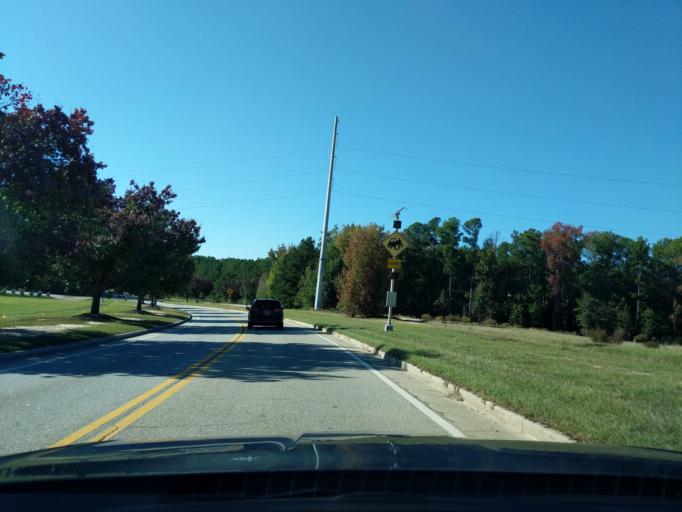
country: US
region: Georgia
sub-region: Columbia County
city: Grovetown
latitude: 33.4660
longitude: -82.1846
